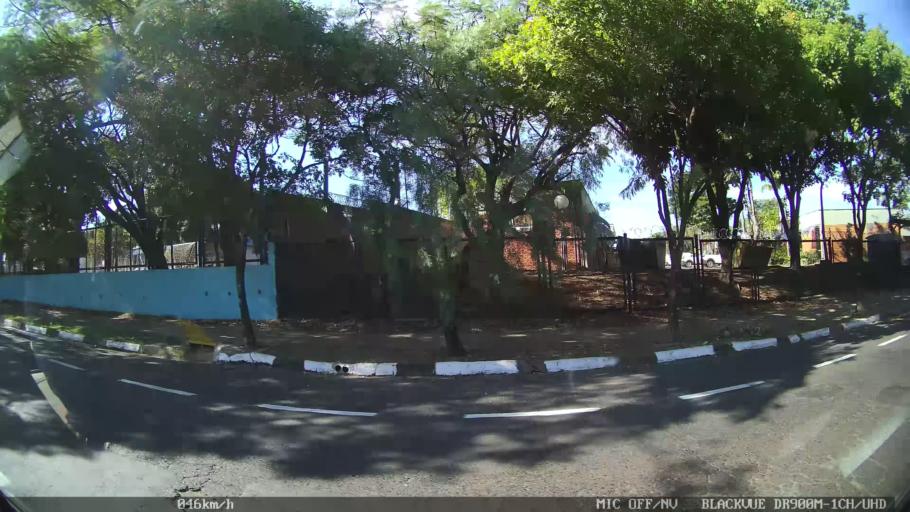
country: BR
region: Sao Paulo
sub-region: Franca
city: Franca
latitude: -20.5083
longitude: -47.4015
